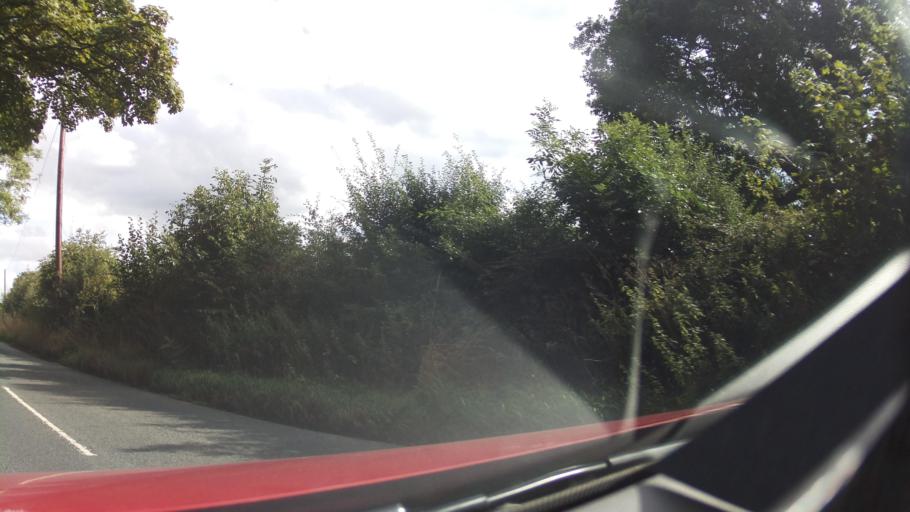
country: GB
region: England
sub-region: North Yorkshire
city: Bedale
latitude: 54.2119
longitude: -1.6231
